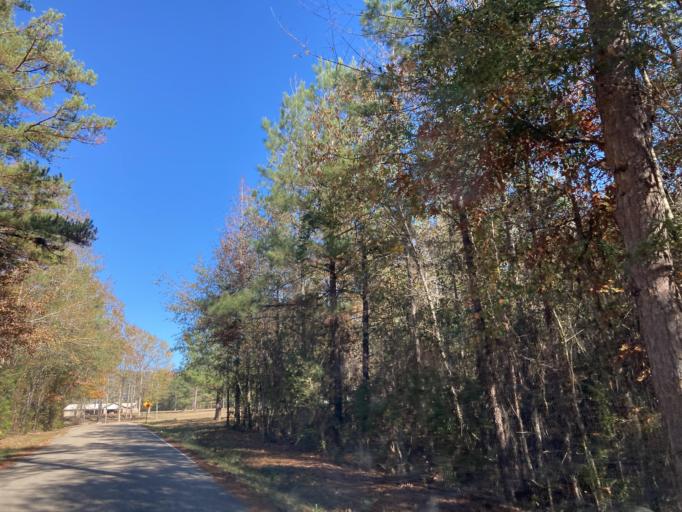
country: US
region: Mississippi
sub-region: Lamar County
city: Sumrall
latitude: 31.2917
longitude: -89.6484
